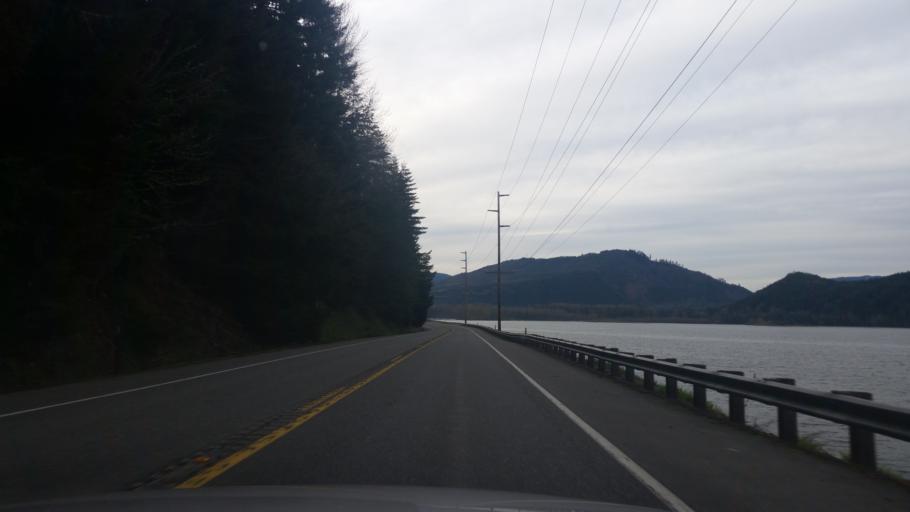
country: US
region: Washington
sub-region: Pierce County
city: Eatonville
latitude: 46.7732
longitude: -122.2167
